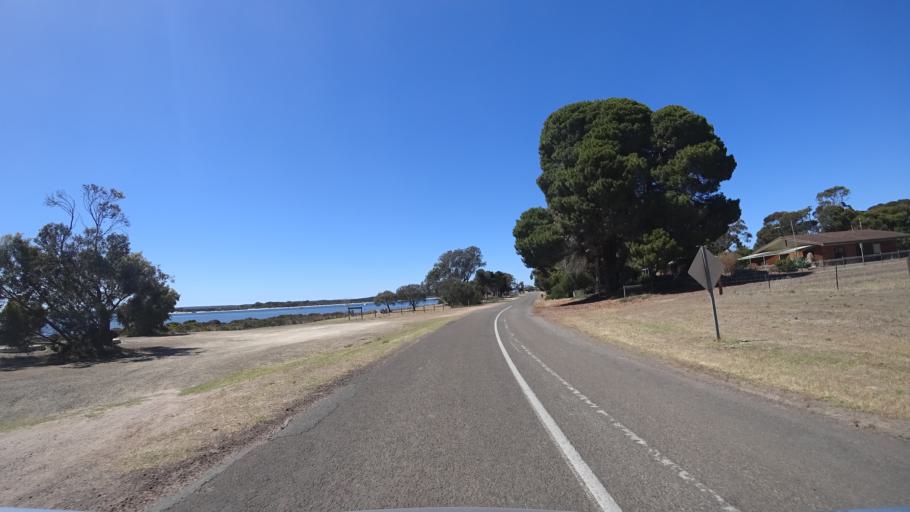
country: AU
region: South Australia
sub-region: Kangaroo Island
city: Kingscote
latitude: -35.7820
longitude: 137.7711
